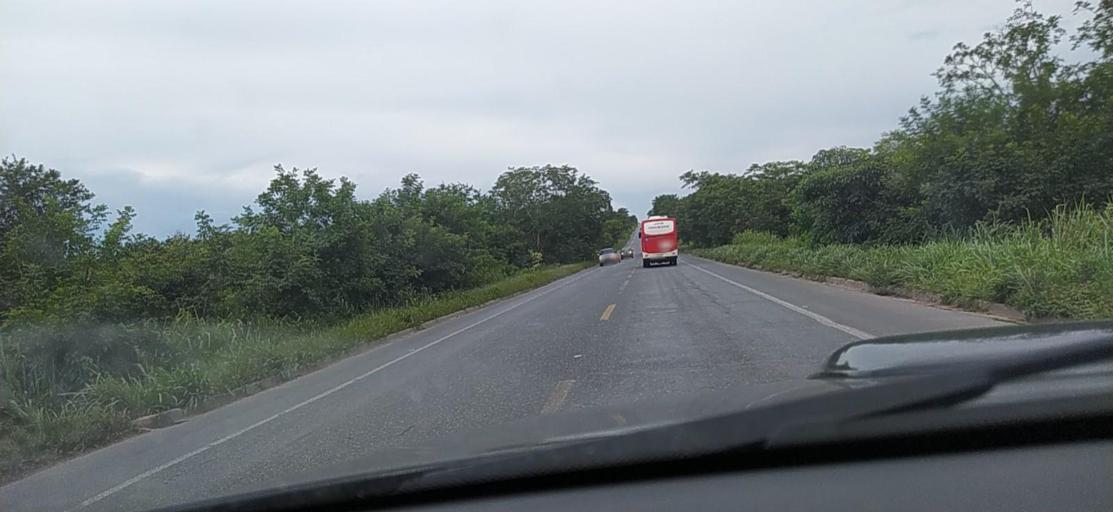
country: BR
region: Minas Gerais
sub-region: Montes Claros
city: Montes Claros
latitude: -16.6636
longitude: -43.7773
